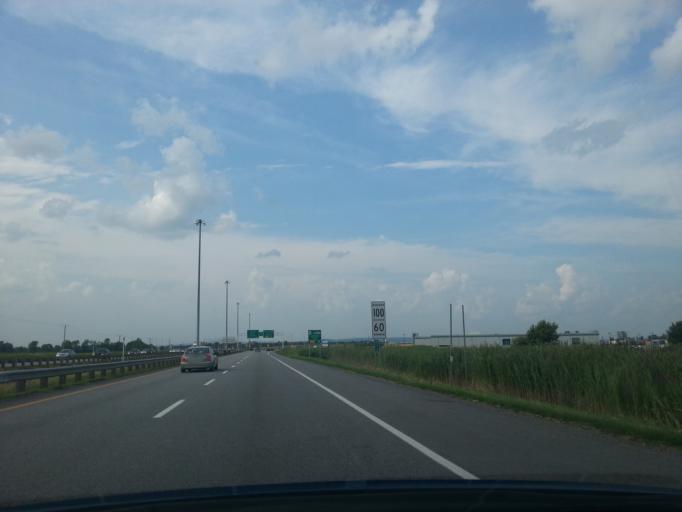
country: CA
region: Quebec
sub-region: Monteregie
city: Vaudreuil-Dorion
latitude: 45.3866
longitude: -74.0572
